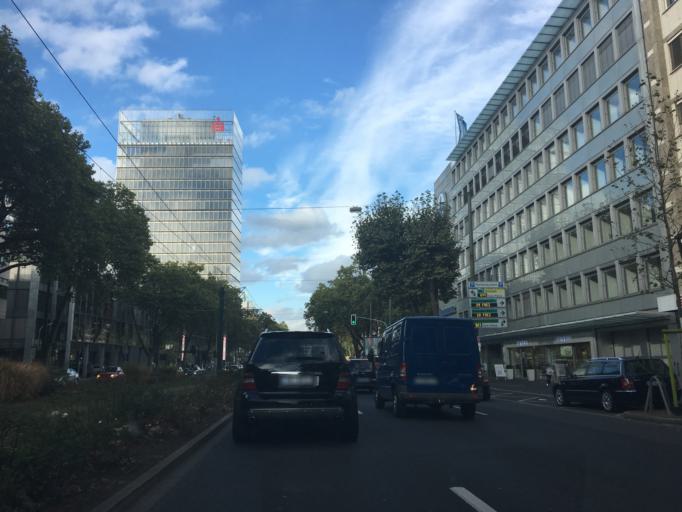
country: DE
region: North Rhine-Westphalia
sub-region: Regierungsbezirk Dusseldorf
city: Dusseldorf
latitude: 51.2208
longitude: 6.7823
